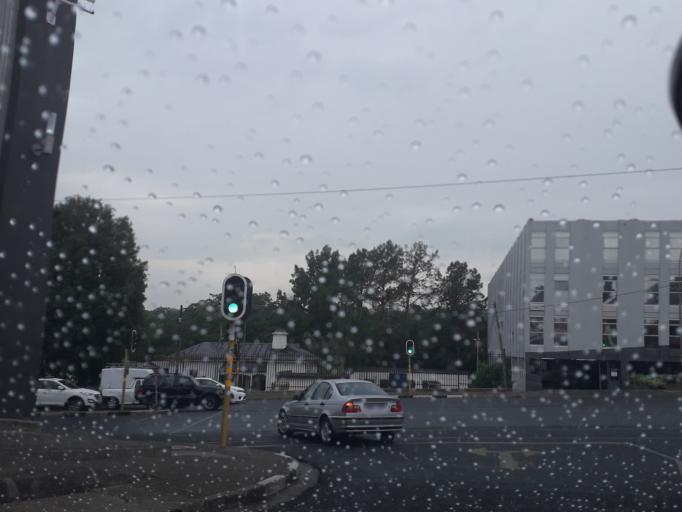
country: ZA
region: Gauteng
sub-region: City of Johannesburg Metropolitan Municipality
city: Johannesburg
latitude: -26.1169
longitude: 28.0239
